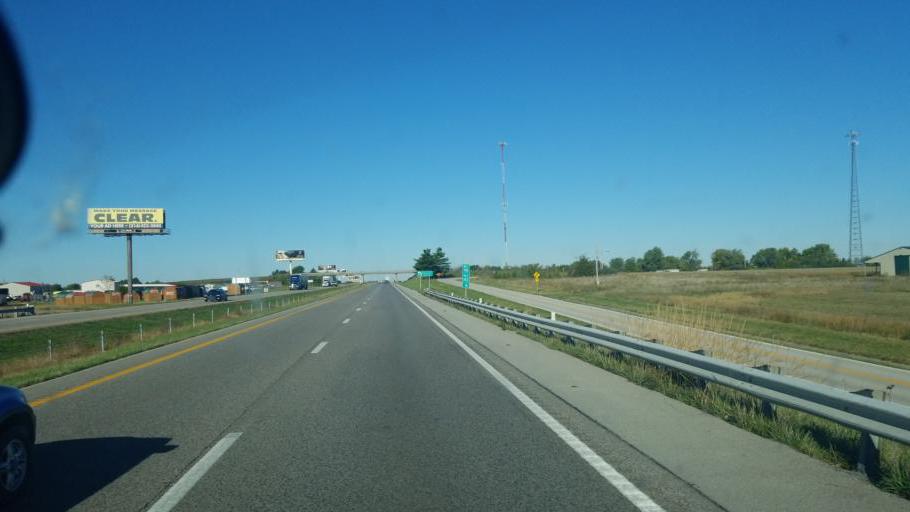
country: US
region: Missouri
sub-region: Warren County
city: Warrenton
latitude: 38.8649
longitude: -91.3267
